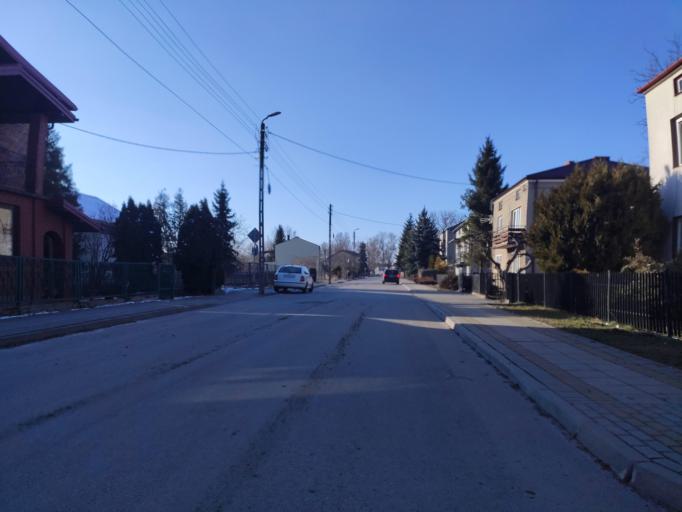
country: PL
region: Lublin Voivodeship
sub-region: Powiat lubartowski
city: Kock
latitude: 51.6421
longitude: 22.4425
